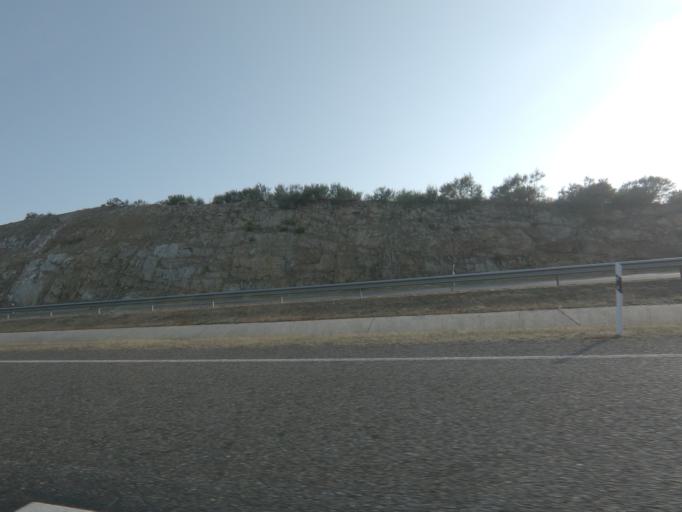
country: ES
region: Galicia
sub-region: Provincia de Ourense
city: Oimbra
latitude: 41.8618
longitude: -7.4265
